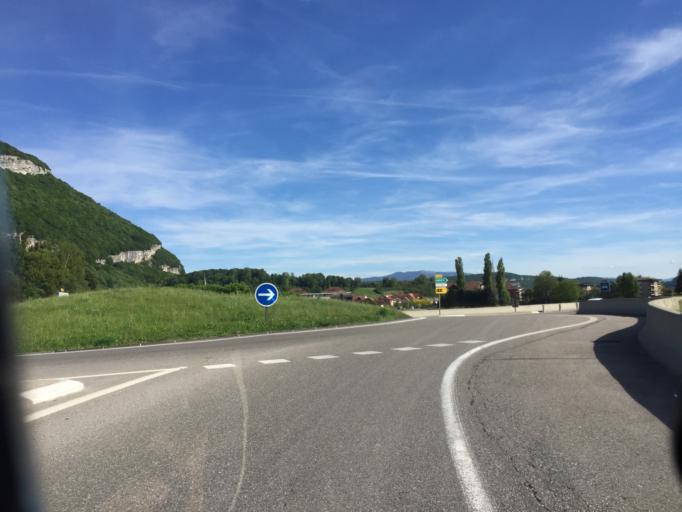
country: FR
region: Rhone-Alpes
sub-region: Departement de la Haute-Savoie
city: La Balme-de-Sillingy
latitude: 45.9647
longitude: 6.0369
